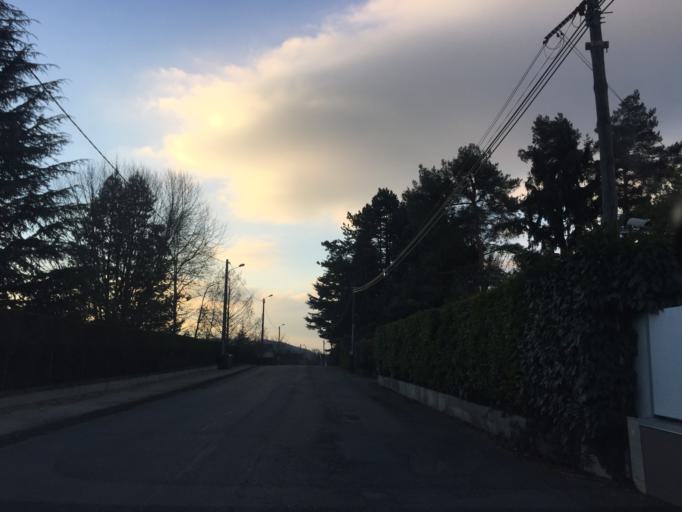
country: FR
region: Rhone-Alpes
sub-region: Departement de la Savoie
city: Tresserve
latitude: 45.6670
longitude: 5.8997
